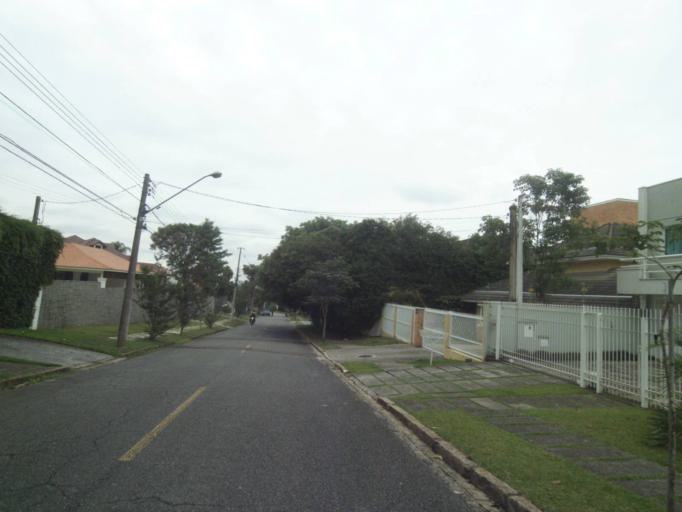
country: BR
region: Parana
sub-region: Curitiba
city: Curitiba
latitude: -25.4061
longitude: -49.2883
